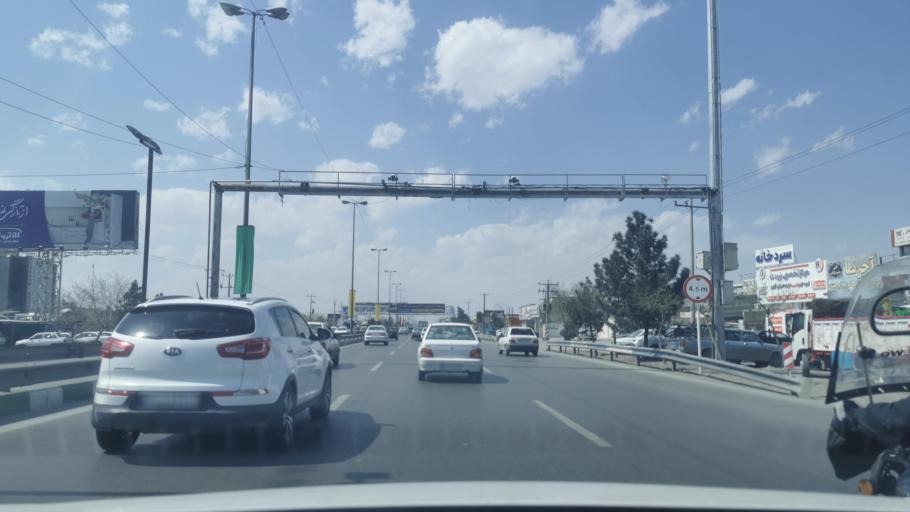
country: IR
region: Razavi Khorasan
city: Mashhad
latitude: 36.3898
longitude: 59.5110
